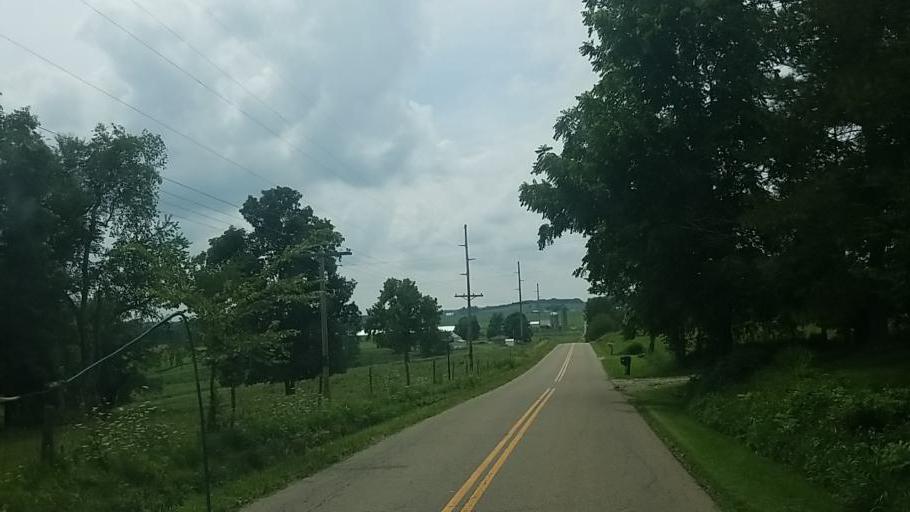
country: US
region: Ohio
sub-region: Knox County
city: Gambier
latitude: 40.3157
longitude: -82.3844
